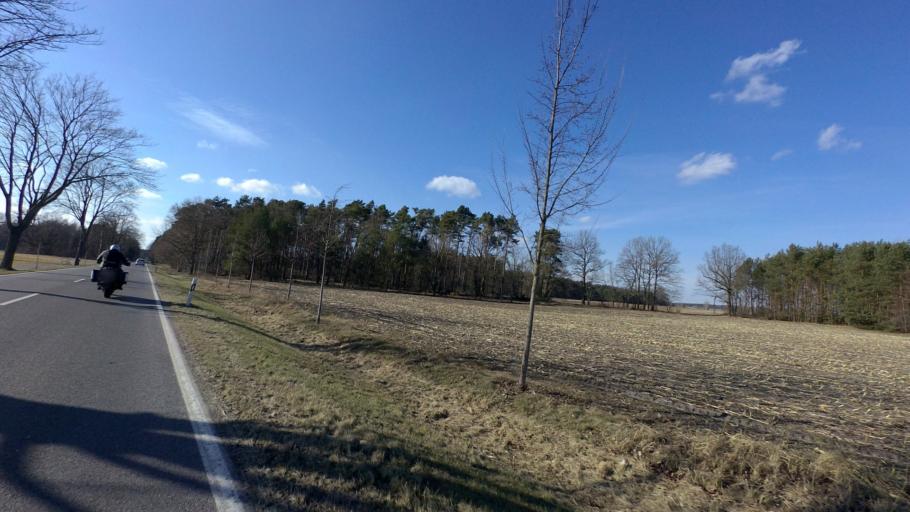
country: DE
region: Brandenburg
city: Birkenwerder
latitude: 52.7597
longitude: 13.3413
